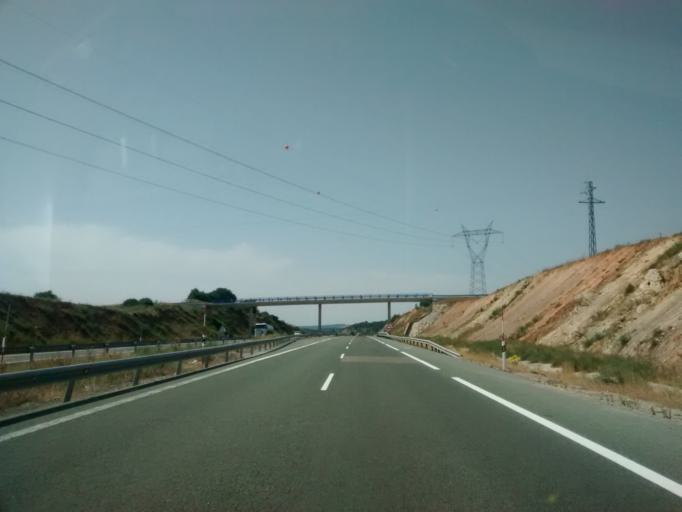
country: ES
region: Cantabria
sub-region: Provincia de Cantabria
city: Mataporquera
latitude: 42.8343
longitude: -4.1978
